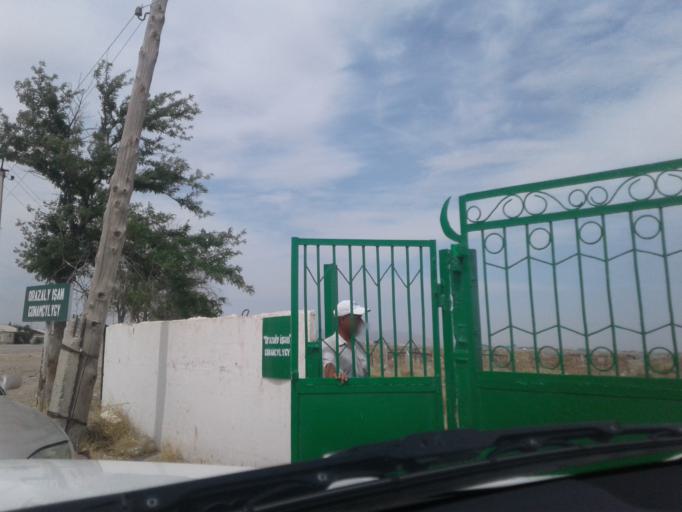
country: TM
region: Balkan
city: Serdar
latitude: 38.9909
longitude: 56.2687
